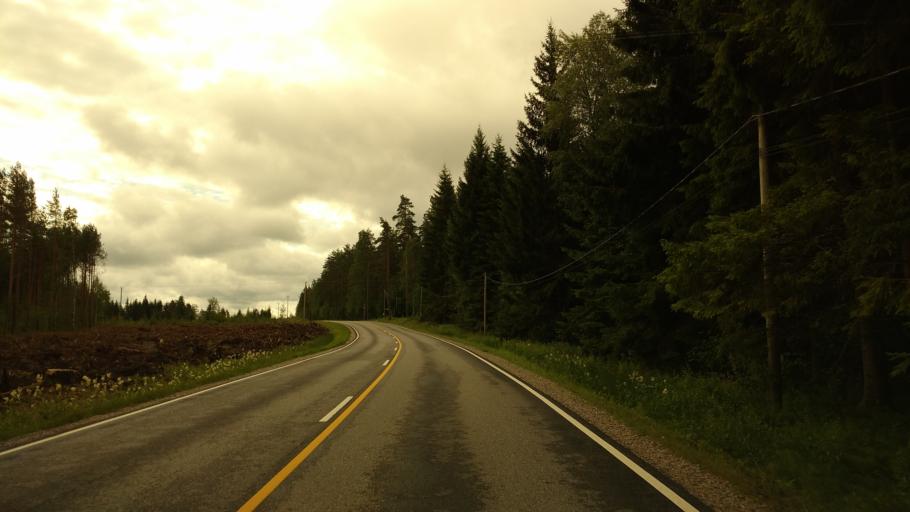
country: FI
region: Varsinais-Suomi
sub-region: Salo
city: Kuusjoki
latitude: 60.4552
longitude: 23.1688
